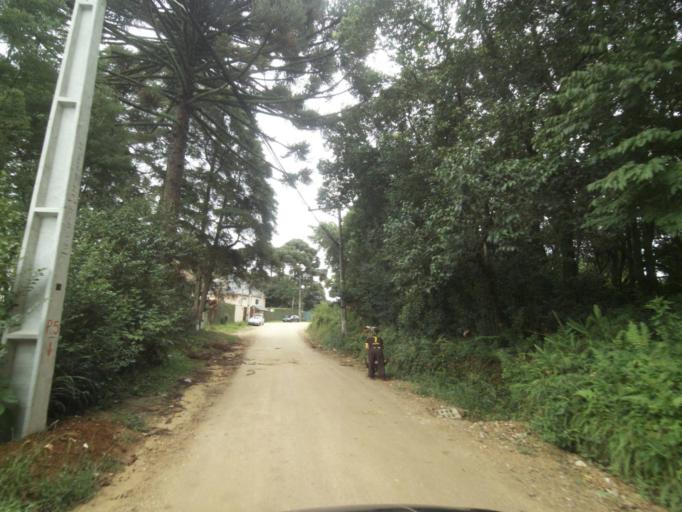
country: BR
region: Parana
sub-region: Curitiba
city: Curitiba
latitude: -25.4708
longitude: -49.3274
